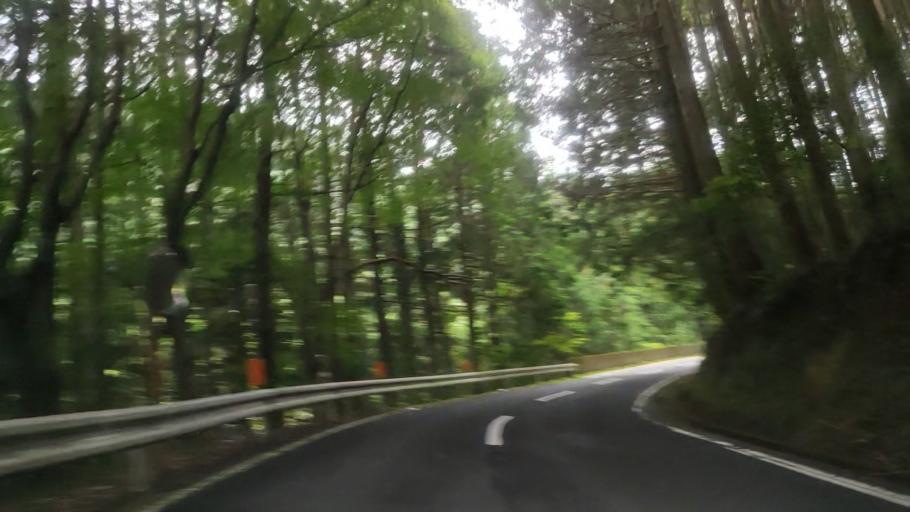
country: JP
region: Wakayama
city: Koya
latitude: 34.2546
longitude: 135.5452
